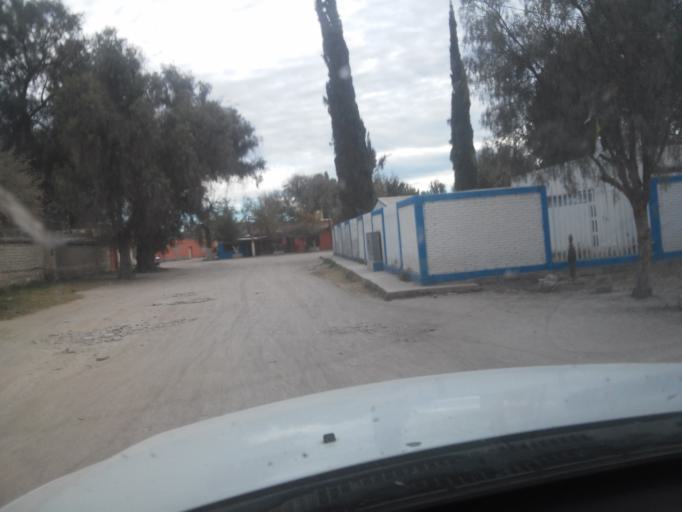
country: MX
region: Durango
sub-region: Durango
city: Jose Refugio Salcido
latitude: 24.0489
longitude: -104.5493
